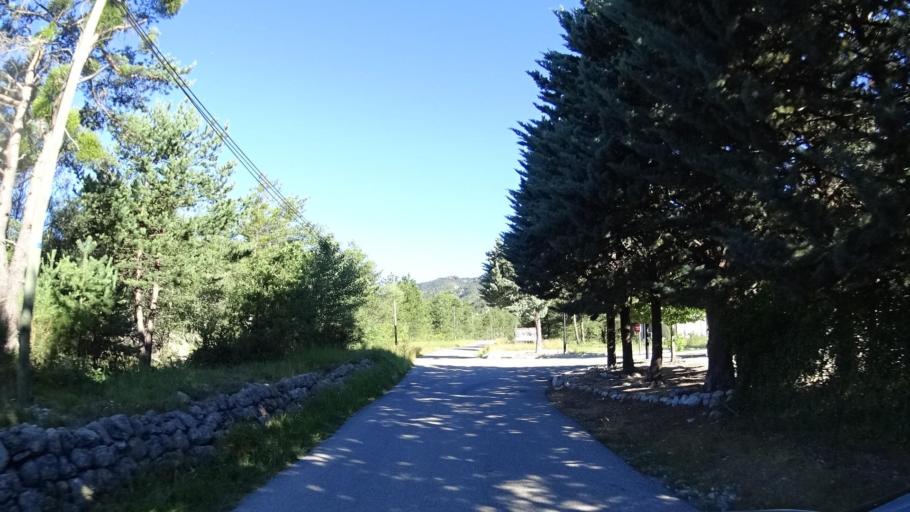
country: FR
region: Provence-Alpes-Cote d'Azur
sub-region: Departement des Alpes-de-Haute-Provence
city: Castellane
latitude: 43.8776
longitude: 6.5048
